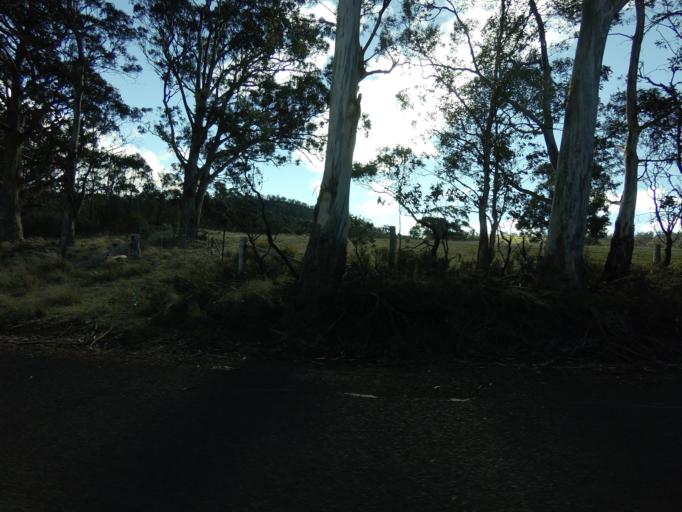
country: AU
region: Tasmania
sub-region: Derwent Valley
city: New Norfolk
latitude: -42.7263
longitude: 147.0304
